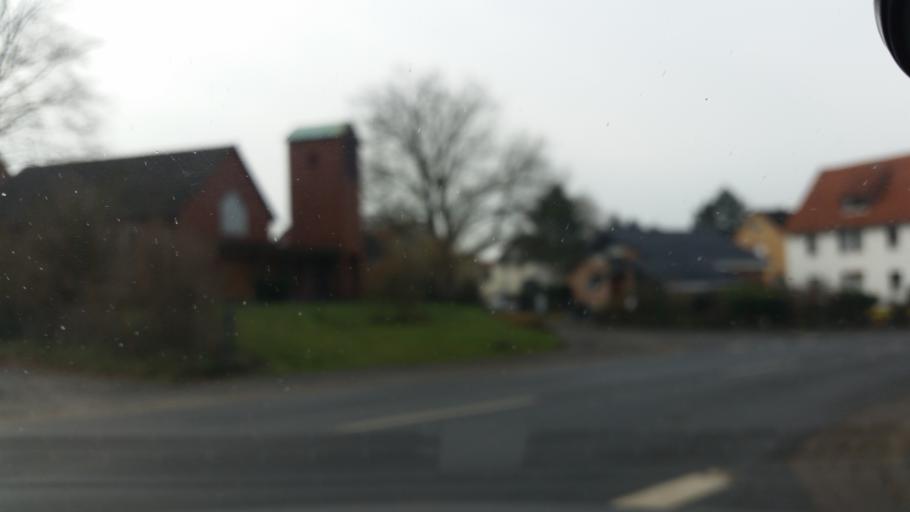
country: DE
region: Lower Saxony
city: Seelze
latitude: 52.3739
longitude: 9.5924
